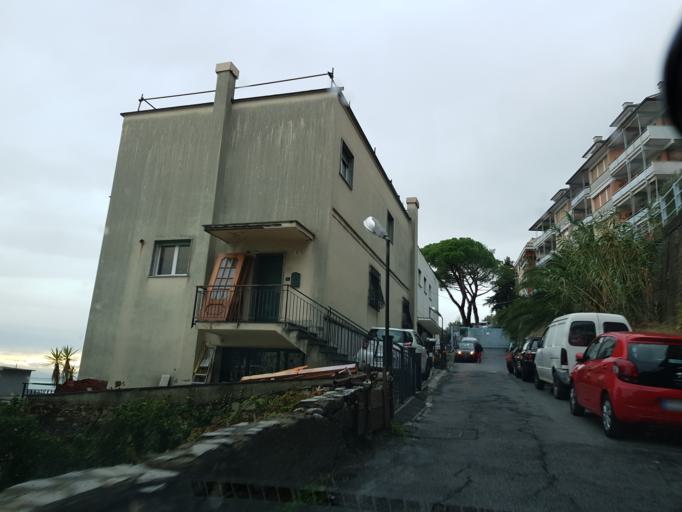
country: IT
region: Liguria
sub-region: Provincia di Genova
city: Bogliasco
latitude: 44.3877
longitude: 9.0211
